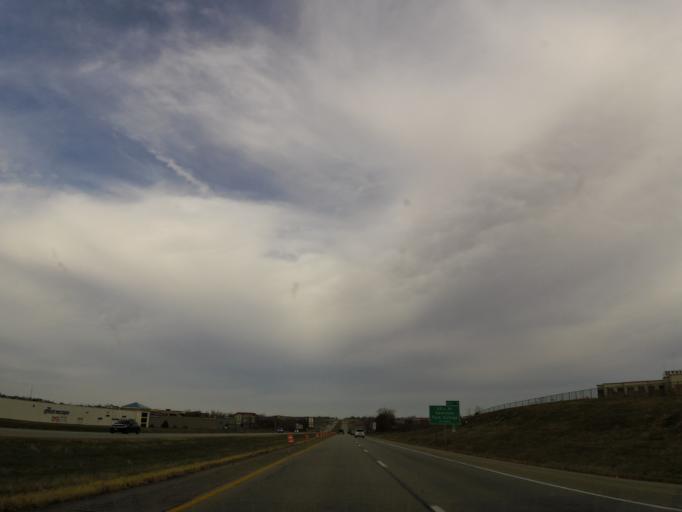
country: US
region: Iowa
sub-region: Scott County
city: Bettendorf
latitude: 41.5640
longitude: -90.5223
